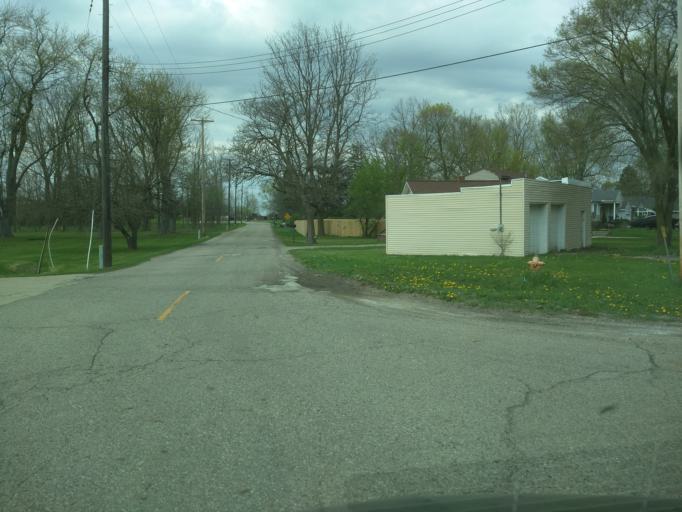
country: US
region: Michigan
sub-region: Eaton County
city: Waverly
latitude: 42.6993
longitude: -84.6228
